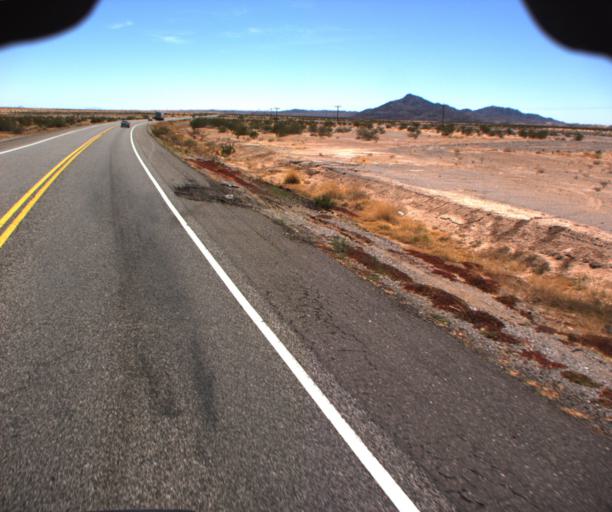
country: US
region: Arizona
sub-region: La Paz County
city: Parker
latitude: 34.0662
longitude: -114.2579
